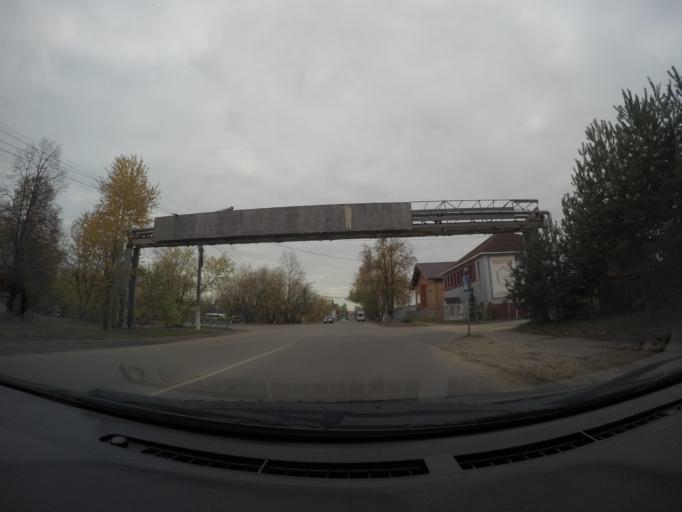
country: RU
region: Moskovskaya
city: Staraya Kupavna
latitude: 55.7995
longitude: 38.1841
